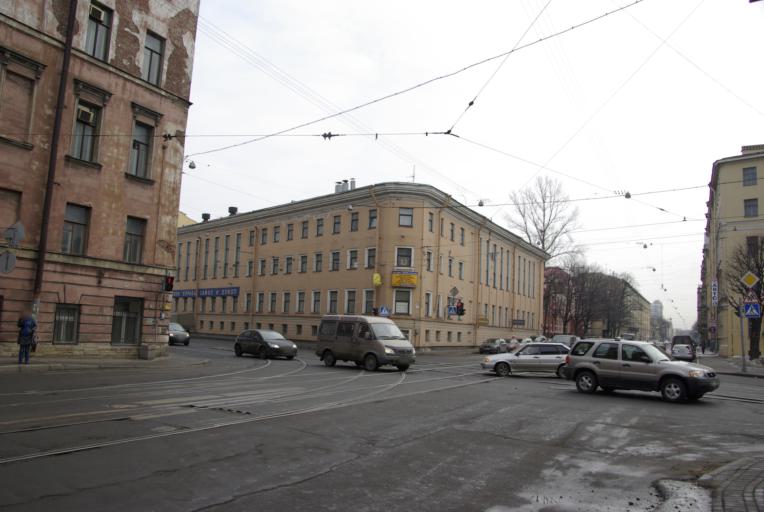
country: RU
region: St.-Petersburg
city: Admiralteisky
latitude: 59.9133
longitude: 30.2771
